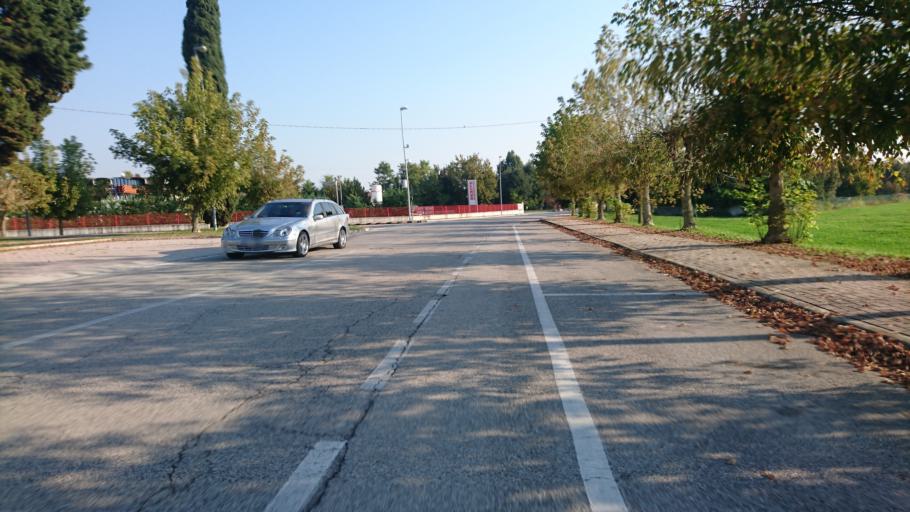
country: IT
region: Veneto
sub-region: Provincia di Padova
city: Grantorto
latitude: 45.5998
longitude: 11.7249
